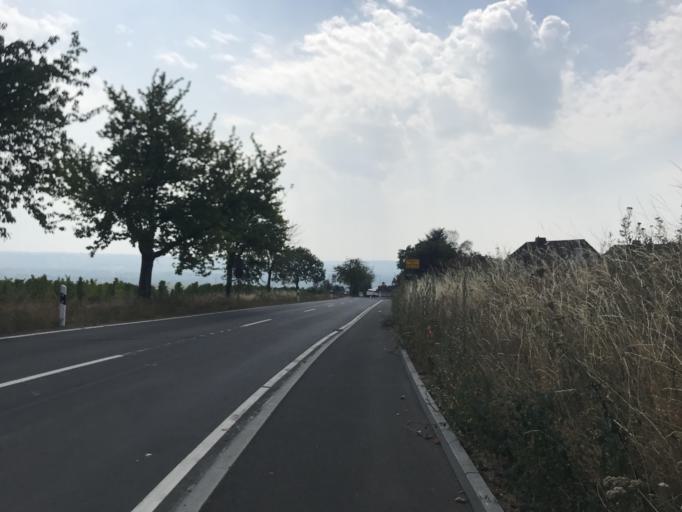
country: DE
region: Rheinland-Pfalz
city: Oestrich-Winkel
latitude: 50.0318
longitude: 8.0329
